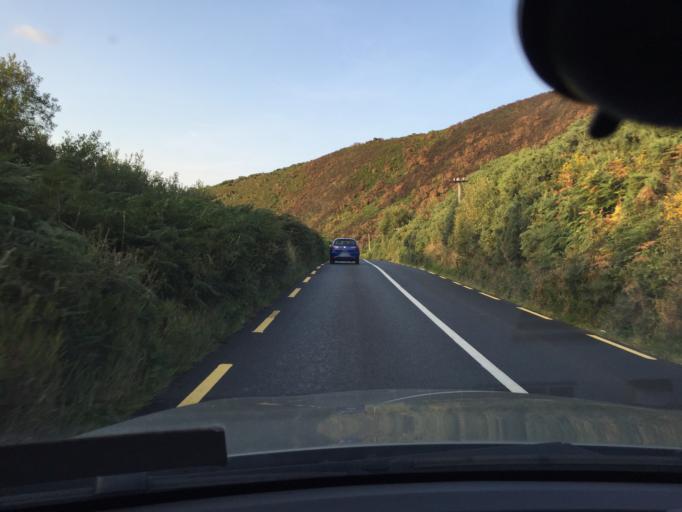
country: IE
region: Leinster
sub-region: Wicklow
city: Rathdrum
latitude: 53.0347
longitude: -6.2496
